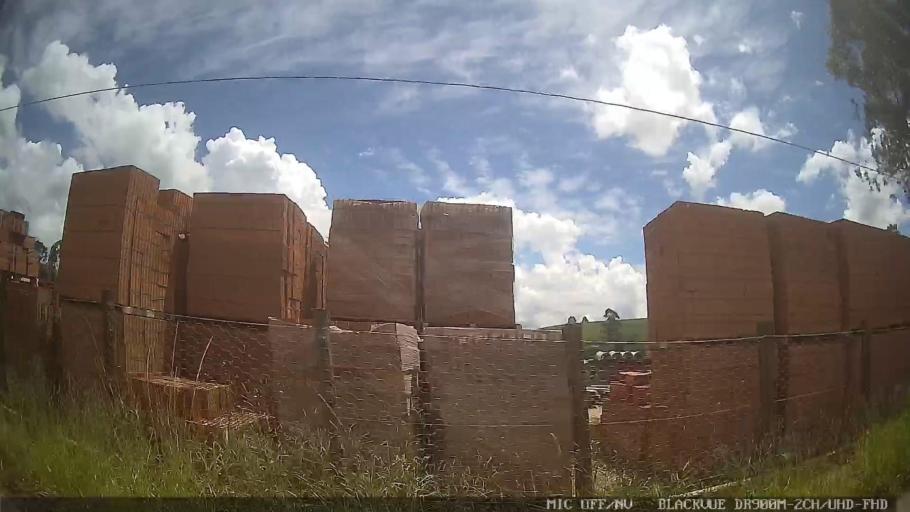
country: BR
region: Minas Gerais
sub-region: Extrema
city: Extrema
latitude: -22.7332
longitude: -46.3801
